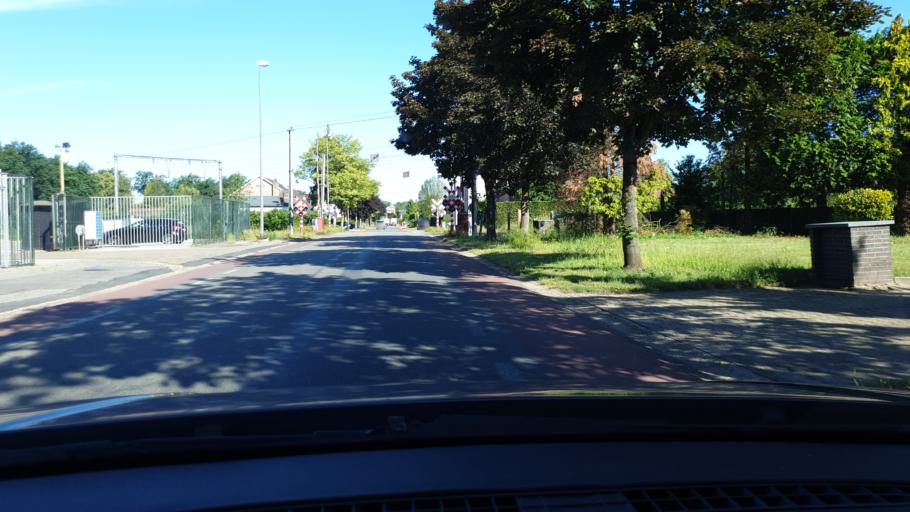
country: BE
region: Flanders
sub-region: Provincie Limburg
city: Hasselt
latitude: 50.9552
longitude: 5.3565
